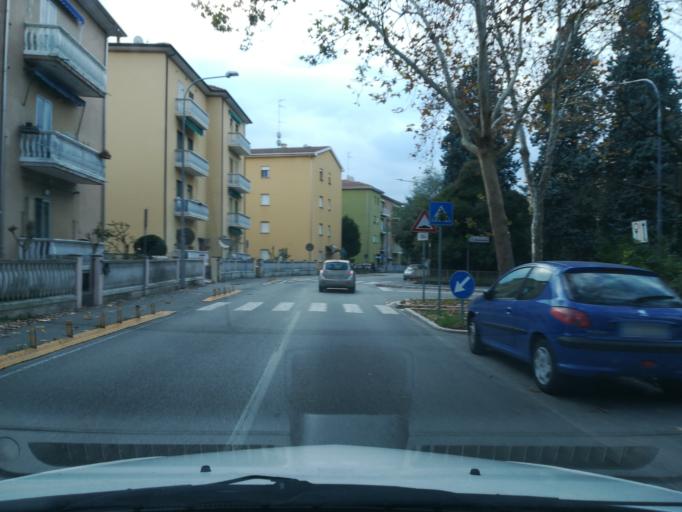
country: IT
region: Emilia-Romagna
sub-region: Provincia di Bologna
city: Imola
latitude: 44.3482
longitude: 11.7188
